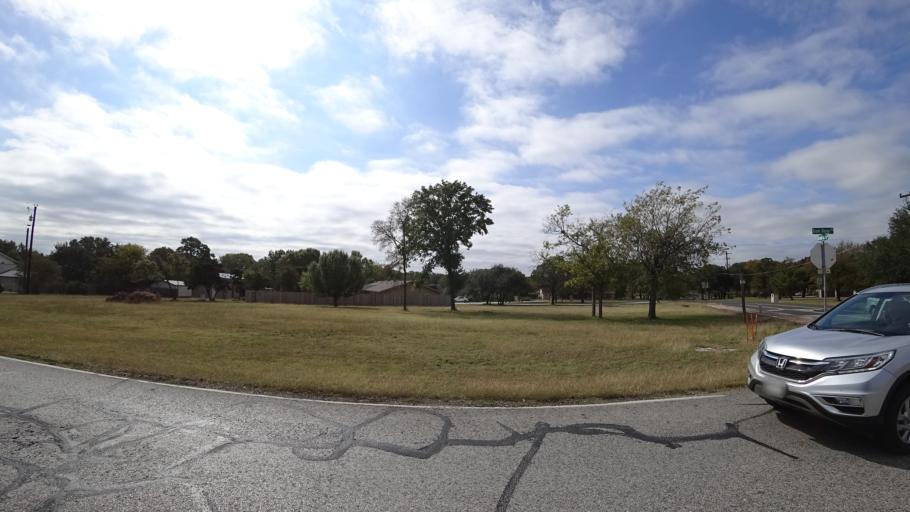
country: US
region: Texas
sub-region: Williamson County
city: Brushy Creek
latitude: 30.5334
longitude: -97.7382
